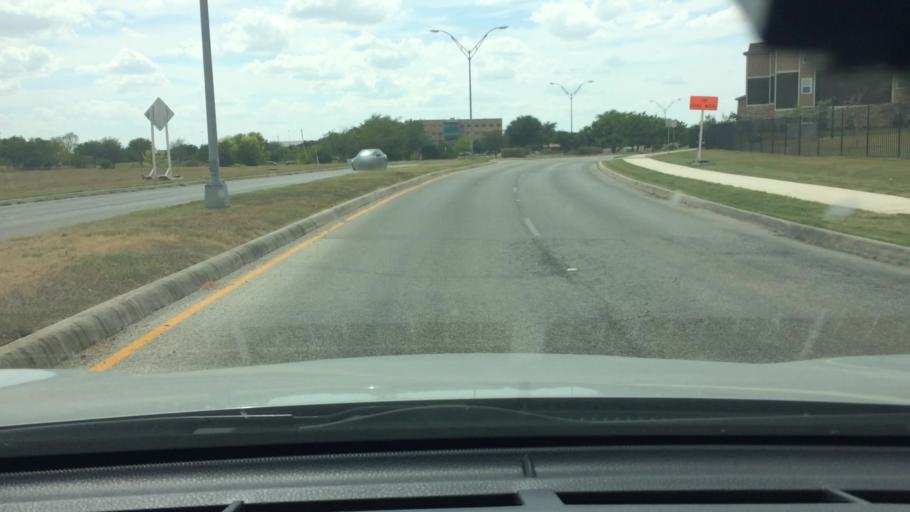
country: US
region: Texas
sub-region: Bexar County
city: China Grove
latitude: 29.3447
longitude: -98.4320
